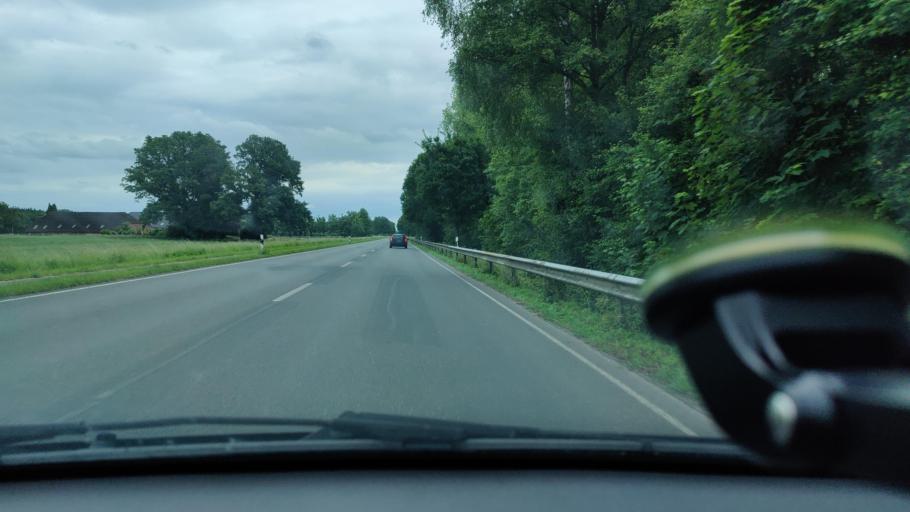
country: DE
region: North Rhine-Westphalia
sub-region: Regierungsbezirk Dusseldorf
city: Weeze
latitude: 51.6672
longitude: 6.2134
